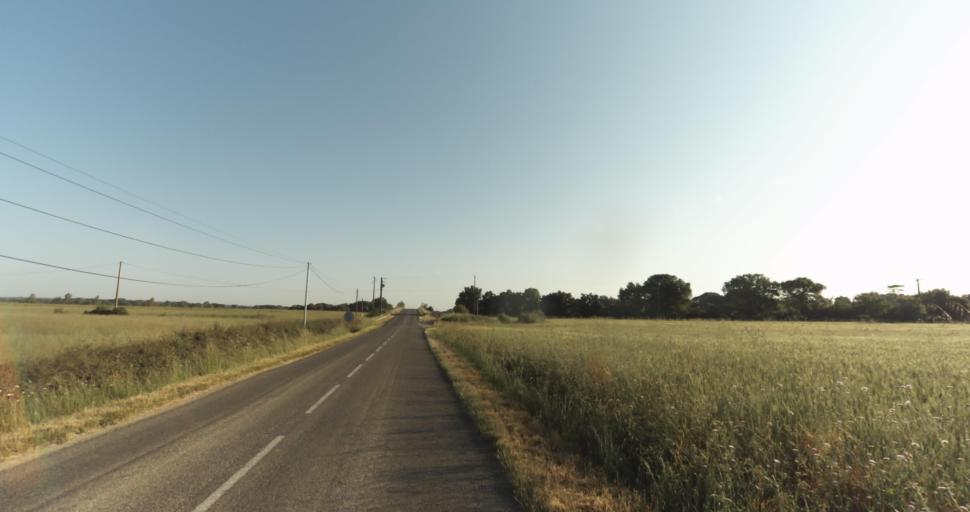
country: FR
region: Midi-Pyrenees
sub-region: Departement de la Haute-Garonne
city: Leguevin
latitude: 43.5787
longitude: 1.2362
